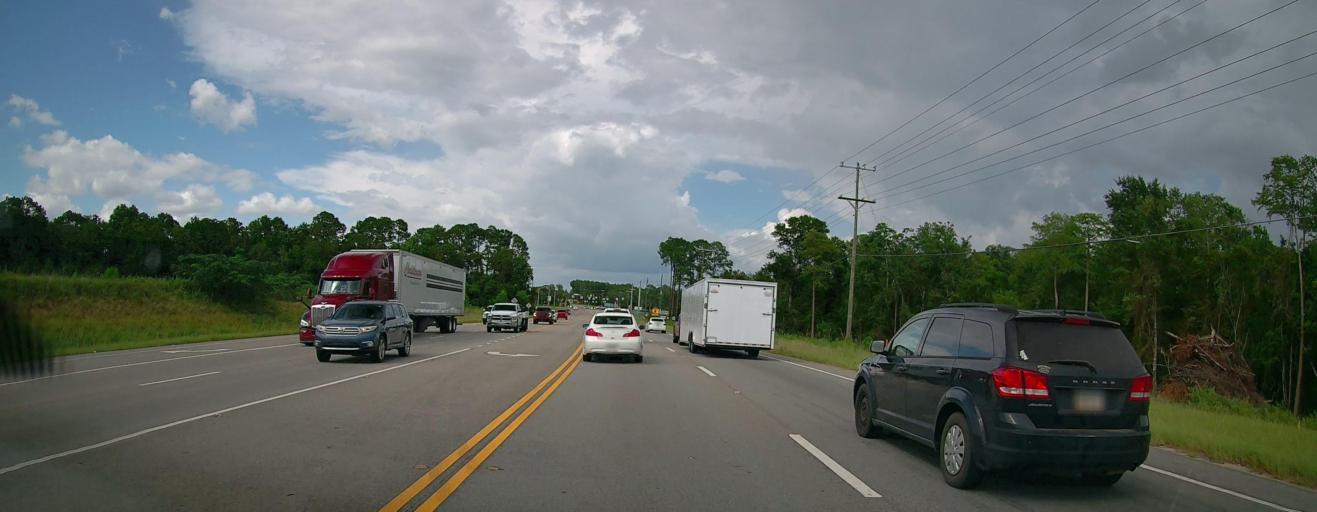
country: US
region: Georgia
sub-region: Coffee County
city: Douglas
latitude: 31.4924
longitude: -82.8317
